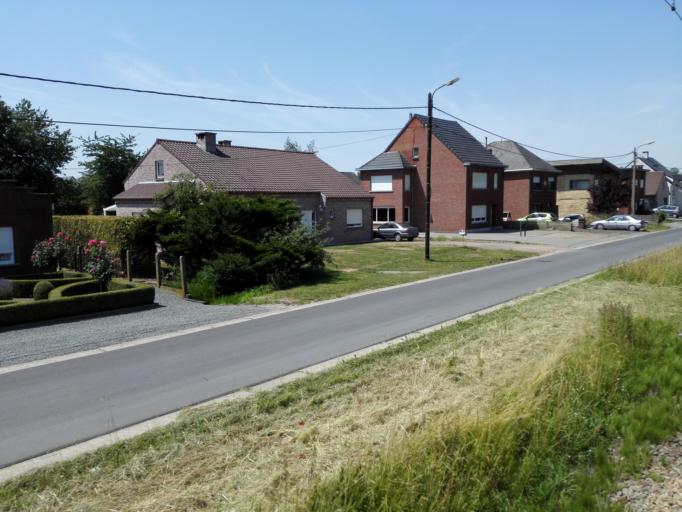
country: BE
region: Flanders
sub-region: Provincie Vlaams-Brabant
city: Begijnendijk
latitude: 51.0397
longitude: 4.7692
